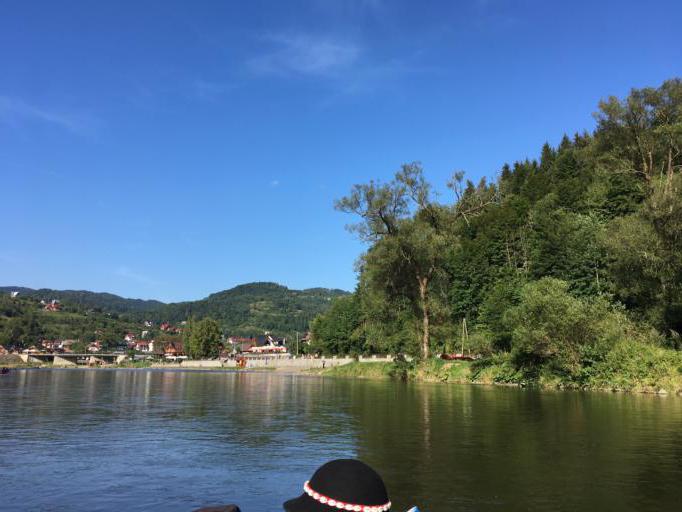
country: PL
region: Lesser Poland Voivodeship
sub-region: Powiat nowotarski
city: Szczawnica
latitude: 49.4211
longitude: 20.4575
